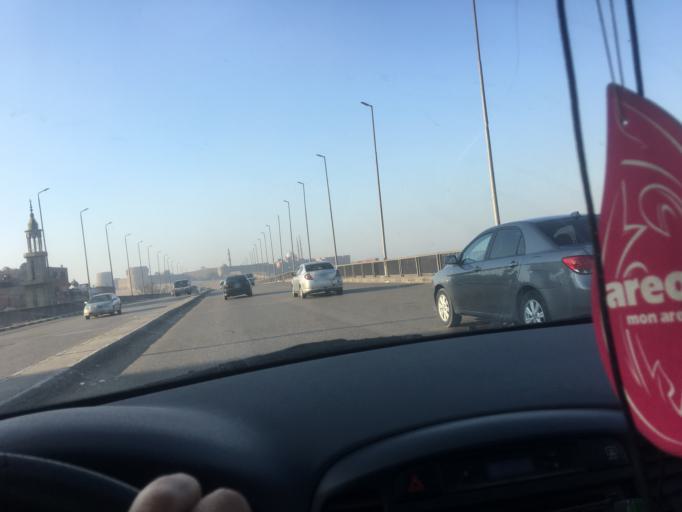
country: EG
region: Muhafazat al Qahirah
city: Cairo
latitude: 30.0364
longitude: 31.2700
